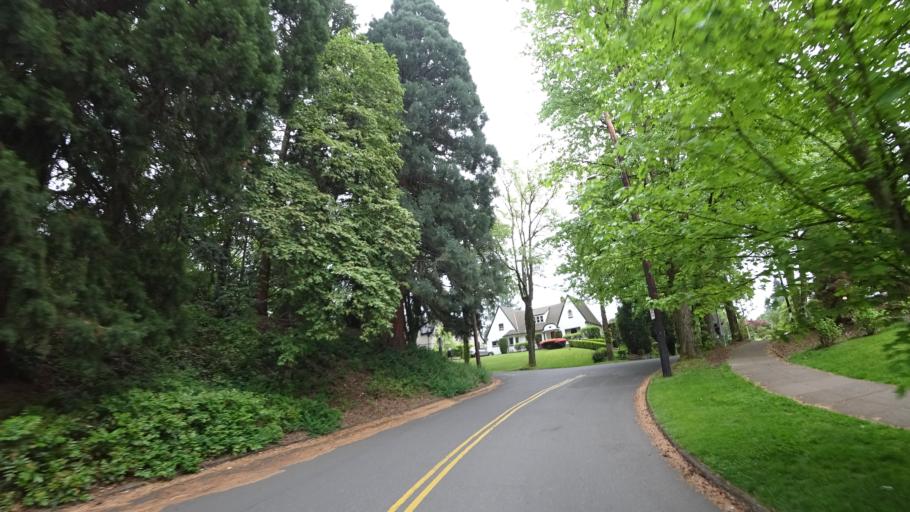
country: US
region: Oregon
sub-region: Multnomah County
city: Portland
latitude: 45.5206
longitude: -122.6309
